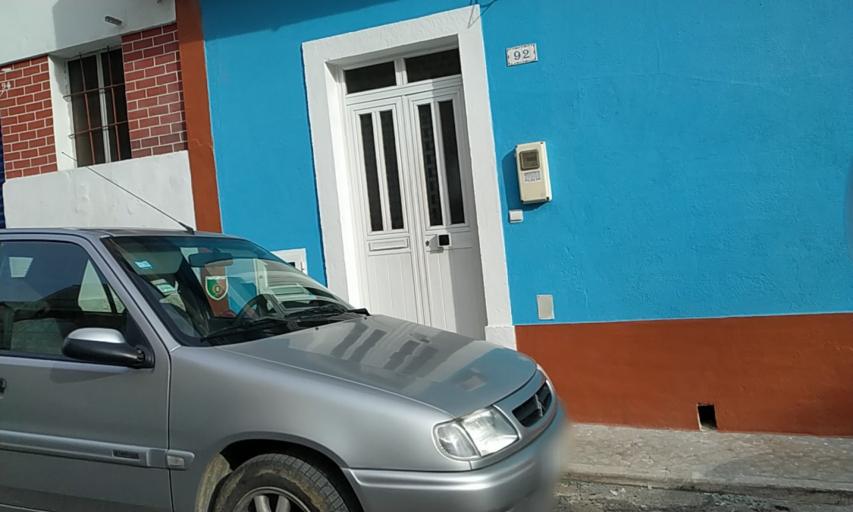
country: PT
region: Setubal
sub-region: Setubal
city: Setubal
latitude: 38.5242
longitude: -8.9028
